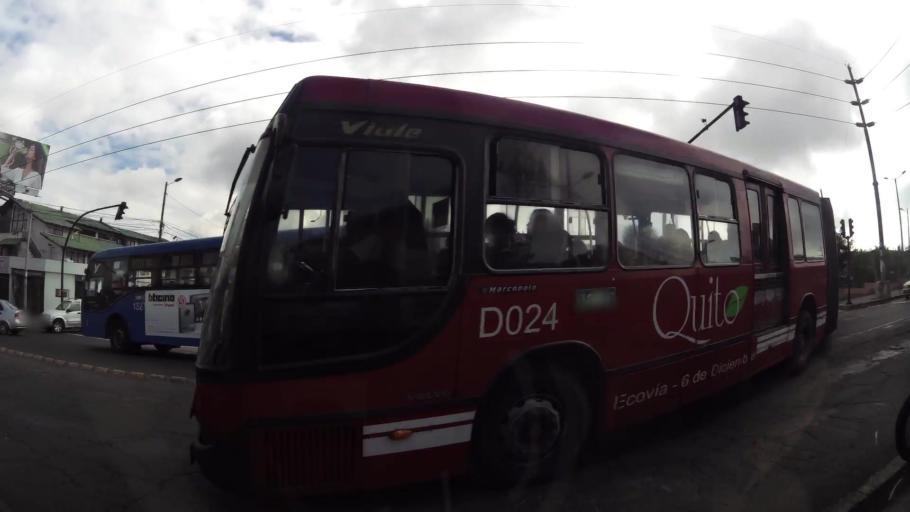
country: EC
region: Pichincha
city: Quito
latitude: -0.1636
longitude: -78.4740
